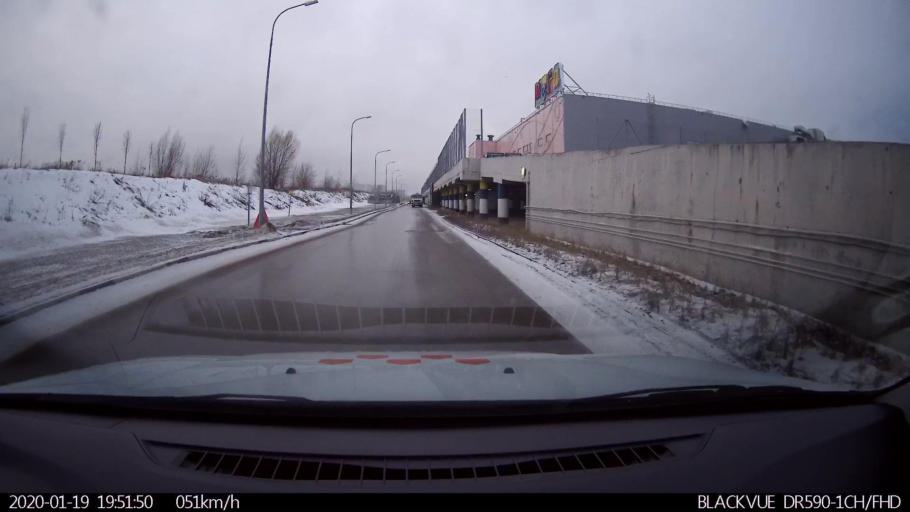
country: RU
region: Nizjnij Novgorod
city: Afonino
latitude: 56.2235
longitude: 44.0692
